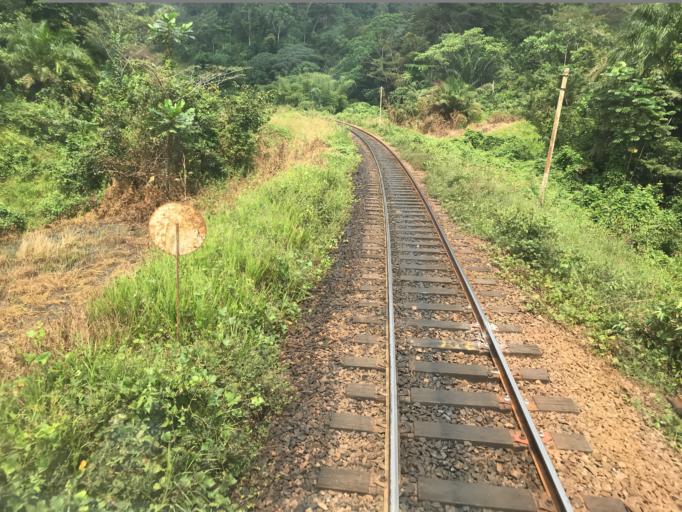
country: CM
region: Centre
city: Eseka
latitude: 3.5781
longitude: 10.9001
